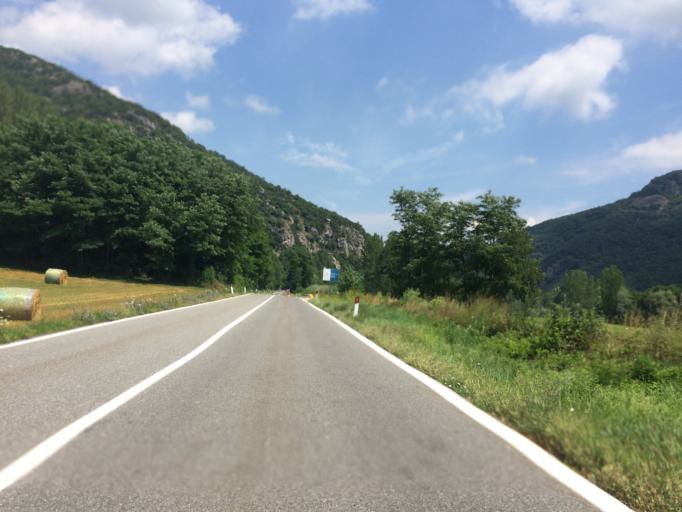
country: IT
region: Piedmont
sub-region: Provincia di Cuneo
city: Priola
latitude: 44.2696
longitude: 8.0297
